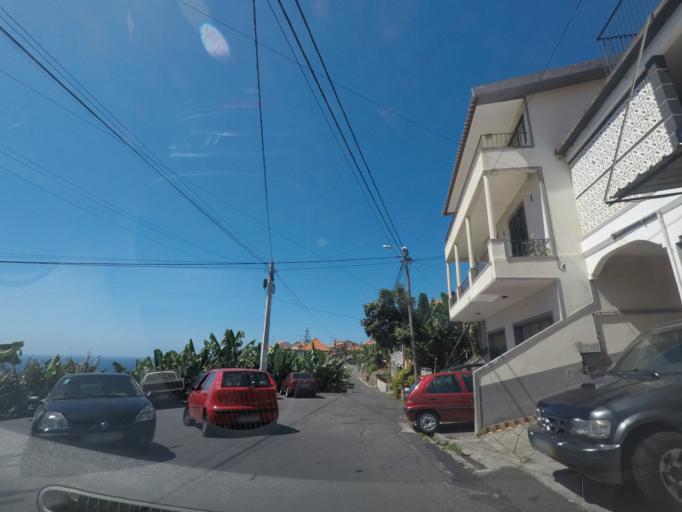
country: PT
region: Madeira
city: Ponta do Sol
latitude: 32.6857
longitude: -17.0958
